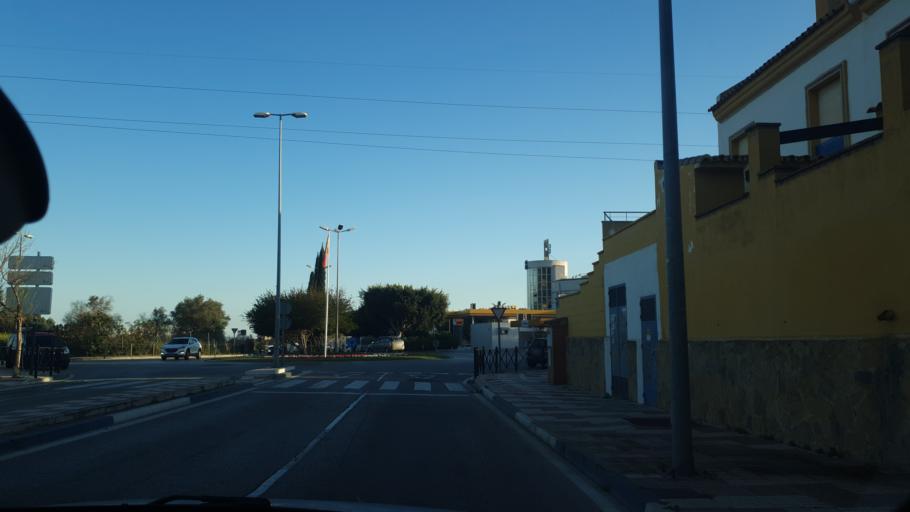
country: ES
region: Andalusia
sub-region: Provincia de Malaga
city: Marbella
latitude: 36.5210
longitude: -4.8920
